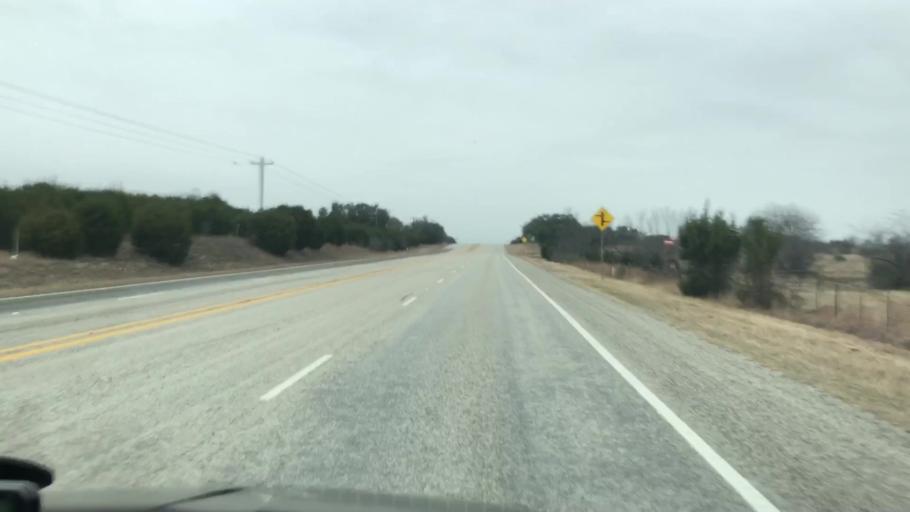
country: US
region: Texas
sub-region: Lampasas County
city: Lampasas
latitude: 31.2310
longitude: -98.1753
